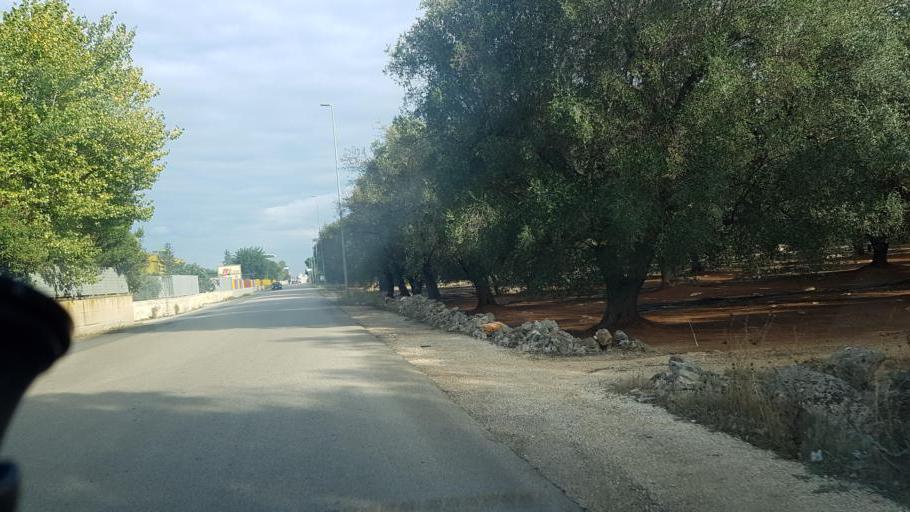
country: IT
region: Apulia
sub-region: Provincia di Brindisi
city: Francavilla Fontana
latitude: 40.5329
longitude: 17.5376
